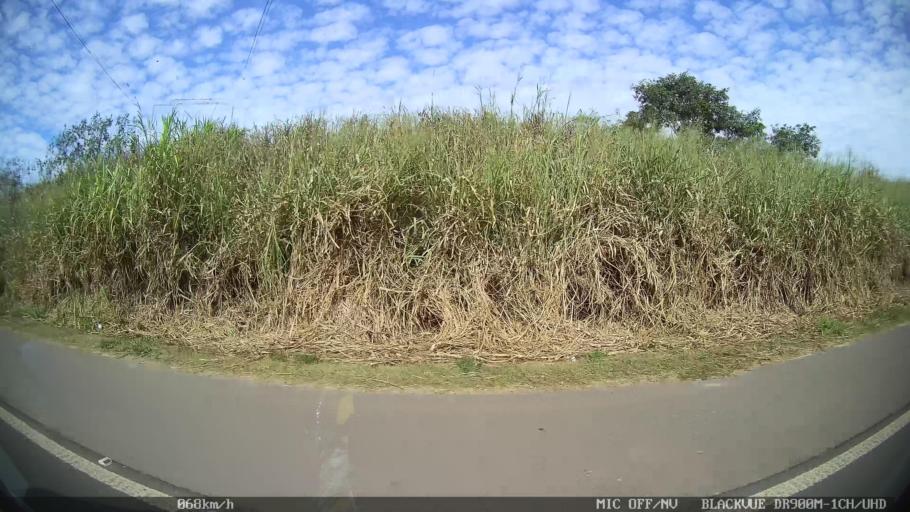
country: BR
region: Sao Paulo
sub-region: Santa Barbara D'Oeste
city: Santa Barbara d'Oeste
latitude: -22.7061
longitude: -47.4483
